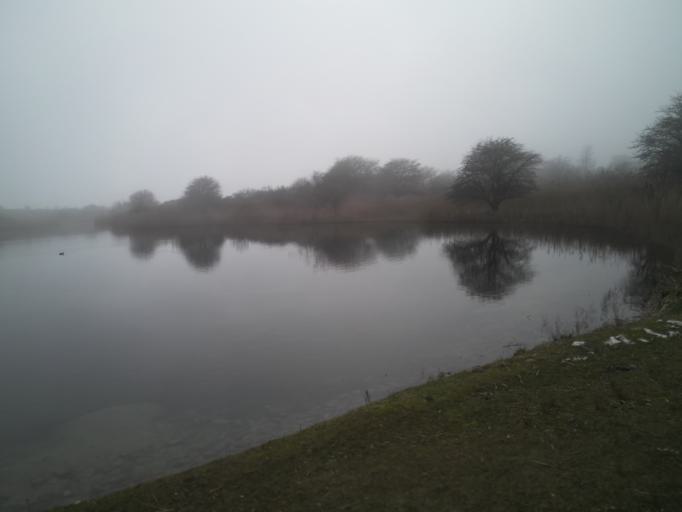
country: NL
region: North Holland
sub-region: Gemeente Zandvoort
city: Zandvoort
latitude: 52.3284
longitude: 4.5316
